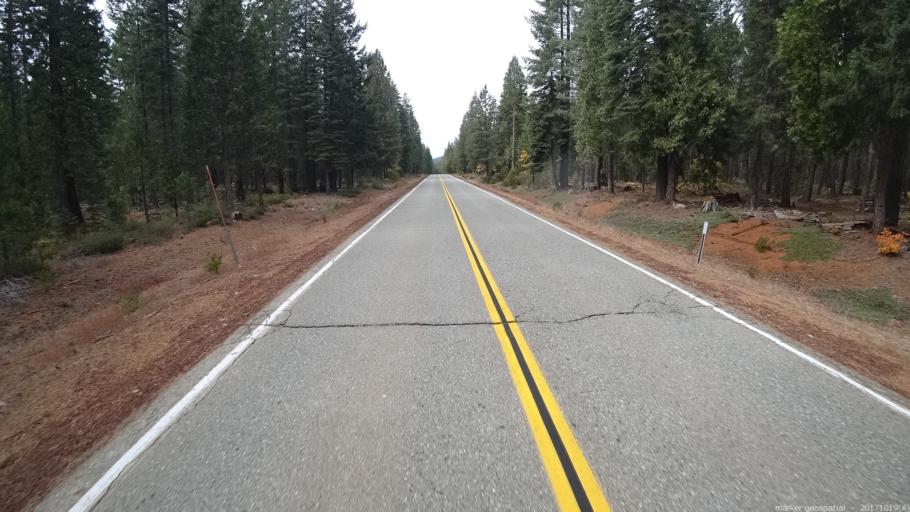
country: US
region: California
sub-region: Shasta County
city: Burney
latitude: 41.1437
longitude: -121.6394
